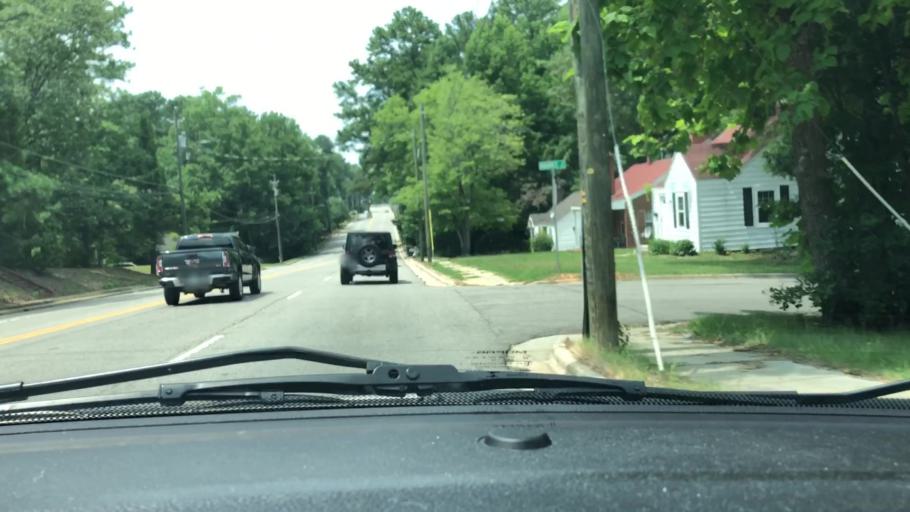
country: US
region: North Carolina
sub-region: Lee County
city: Sanford
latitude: 35.4863
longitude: -79.1859
